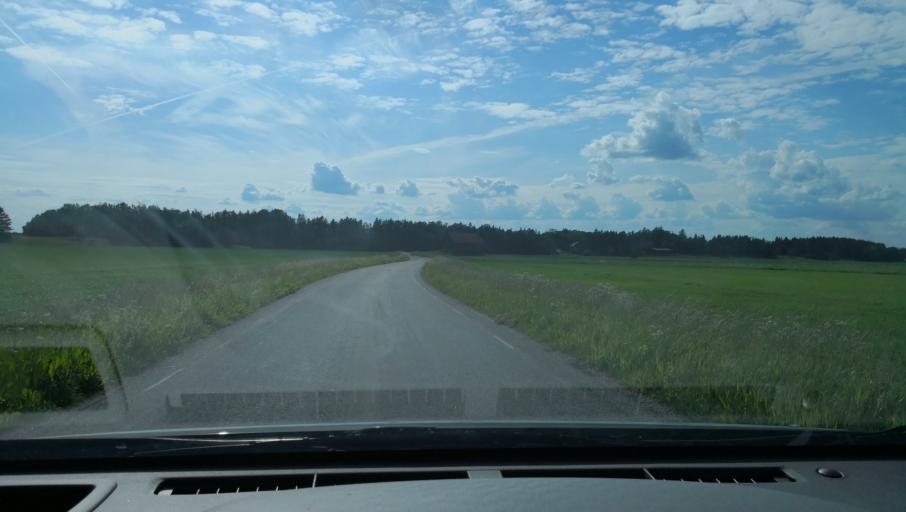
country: SE
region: Uppsala
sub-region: Enkopings Kommun
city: Irsta
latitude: 59.7526
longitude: 16.9624
